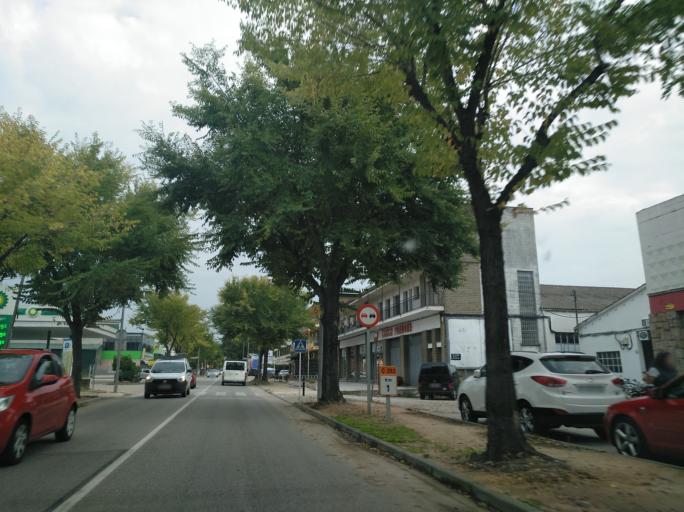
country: ES
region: Catalonia
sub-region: Provincia de Girona
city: Santa Coloma de Farners
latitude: 41.8581
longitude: 2.6730
